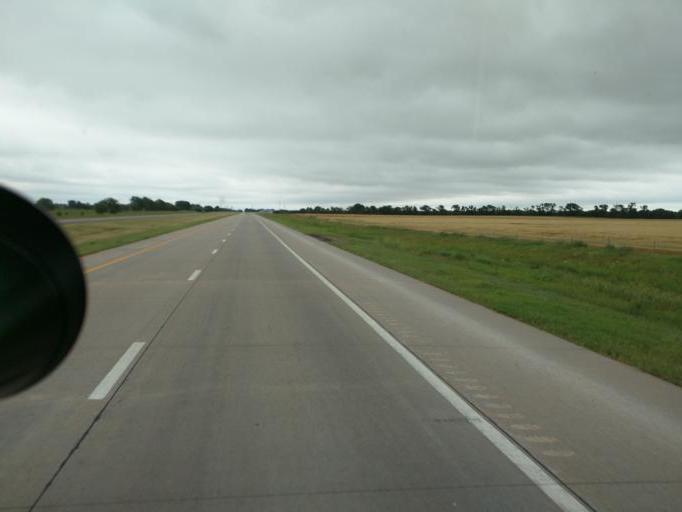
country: US
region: Kansas
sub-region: Reno County
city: South Hutchinson
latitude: 37.9520
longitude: -97.8962
